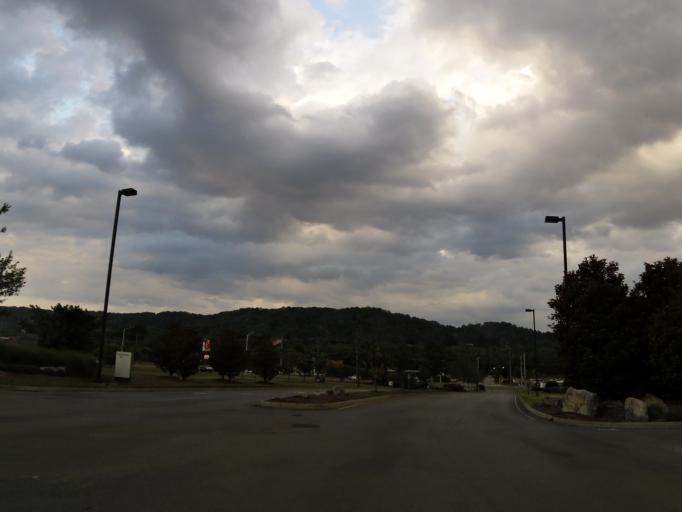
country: US
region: Tennessee
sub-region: Knox County
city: Knoxville
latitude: 36.0519
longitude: -83.9952
